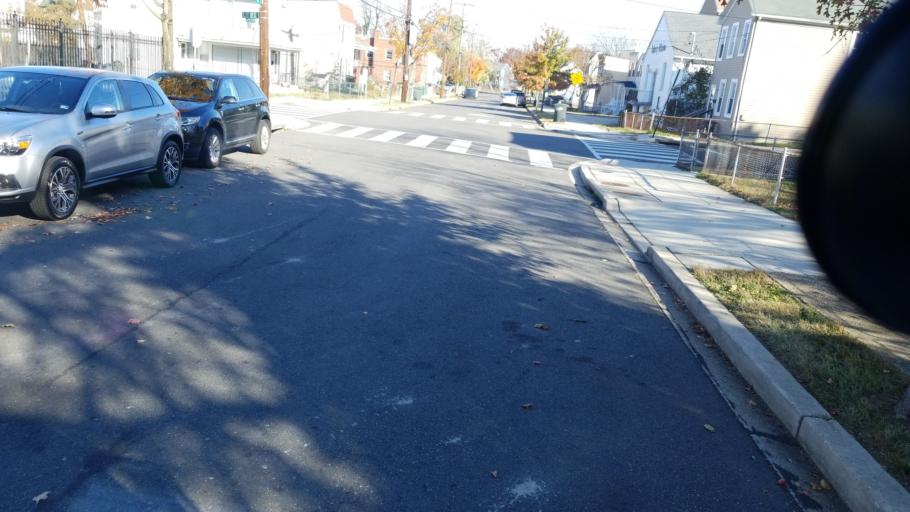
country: US
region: Maryland
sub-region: Prince George's County
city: Fairmount Heights
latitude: 38.9045
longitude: -76.9363
